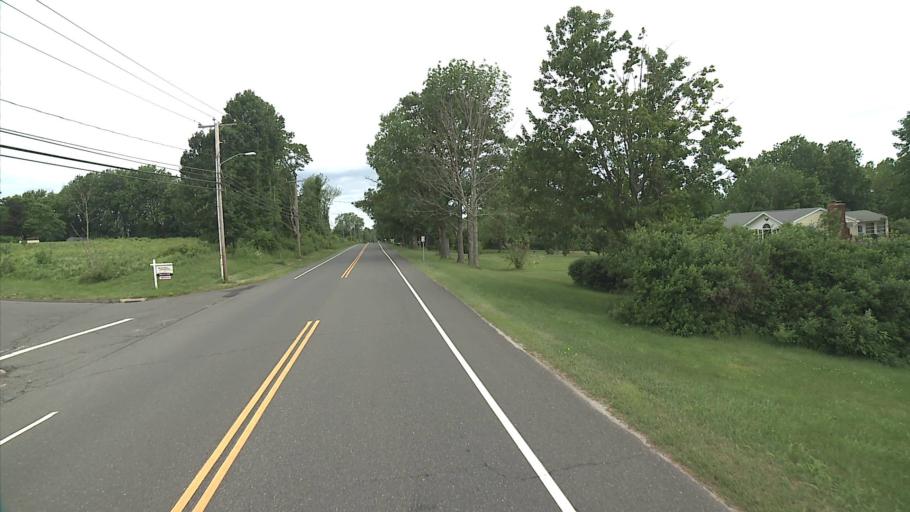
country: US
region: Connecticut
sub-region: Litchfield County
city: Watertown
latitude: 41.6426
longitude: -73.1463
